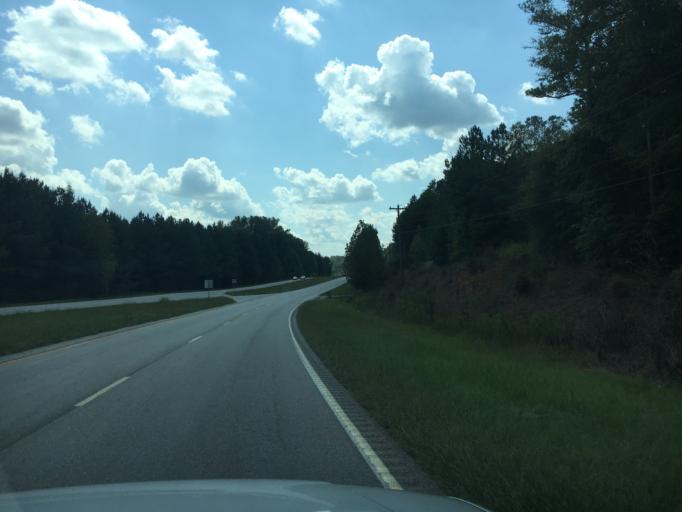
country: US
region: South Carolina
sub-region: Spartanburg County
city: Roebuck
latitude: 34.8197
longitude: -81.9961
